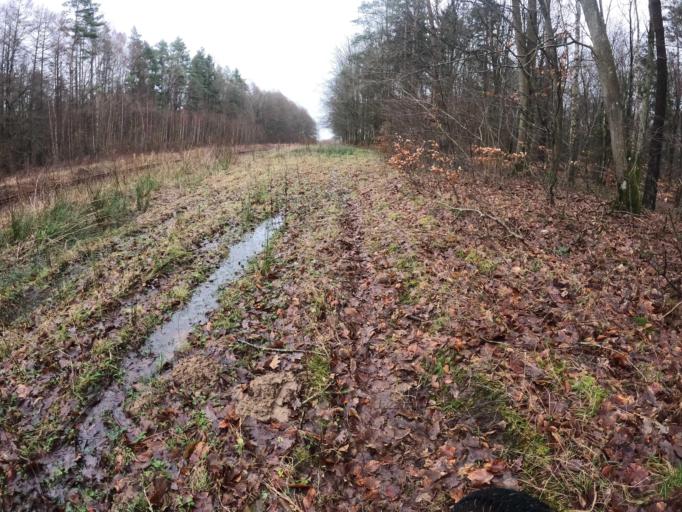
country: PL
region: West Pomeranian Voivodeship
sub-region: Powiat slawienski
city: Darlowo
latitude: 54.3959
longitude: 16.5125
